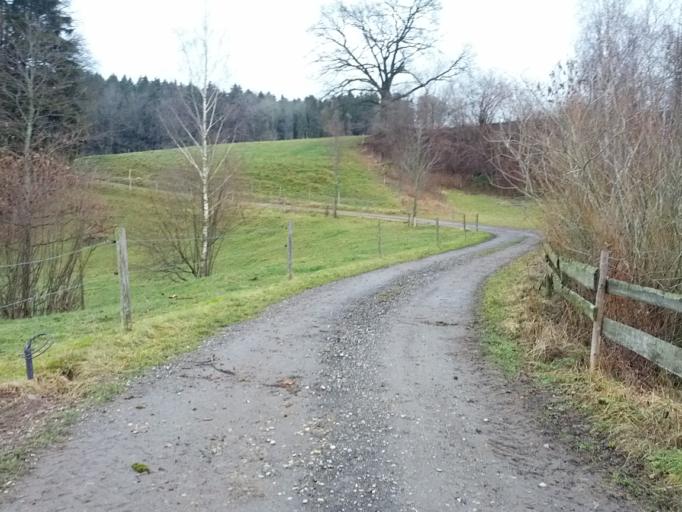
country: DE
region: Baden-Wuerttemberg
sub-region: Tuebingen Region
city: Steinhausen an der Rottum
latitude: 47.9858
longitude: 9.9720
